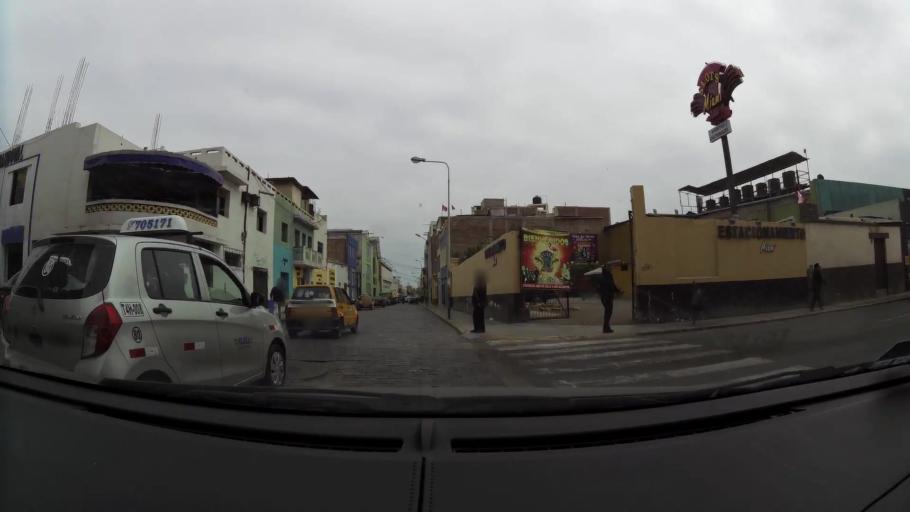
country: PE
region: La Libertad
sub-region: Provincia de Trujillo
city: Trujillo
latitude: -8.1142
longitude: -79.0254
